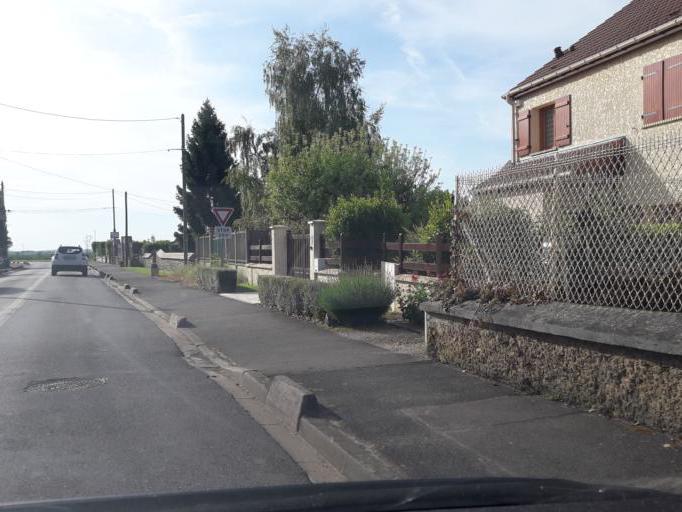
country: FR
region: Ile-de-France
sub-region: Departement de l'Essonne
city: Leudeville
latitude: 48.5648
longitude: 2.3295
